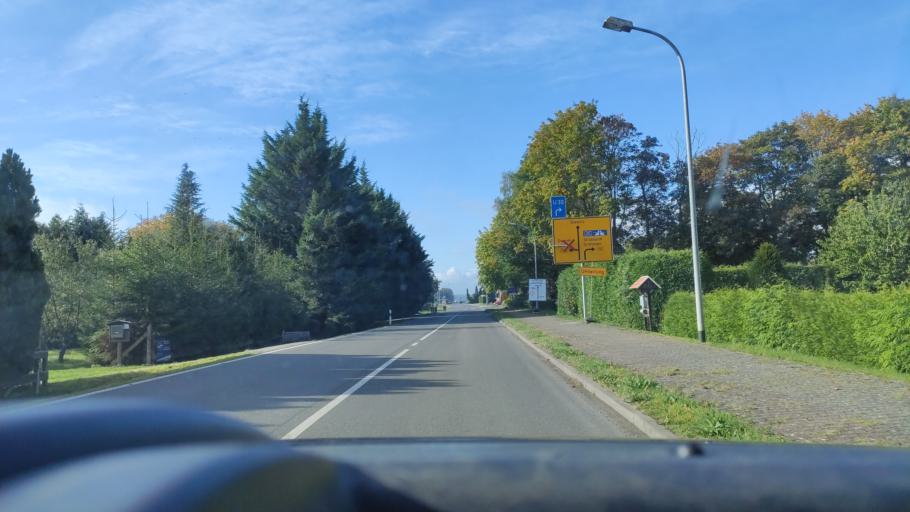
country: DE
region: Mecklenburg-Vorpommern
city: Grimmen
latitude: 54.0539
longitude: 13.1217
